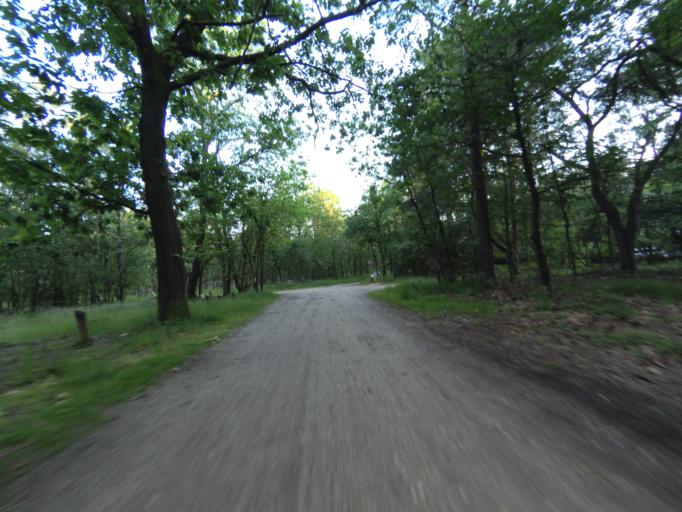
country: NL
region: Gelderland
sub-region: Gemeente Apeldoorn
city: Beekbergen
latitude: 52.1341
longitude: 5.8955
